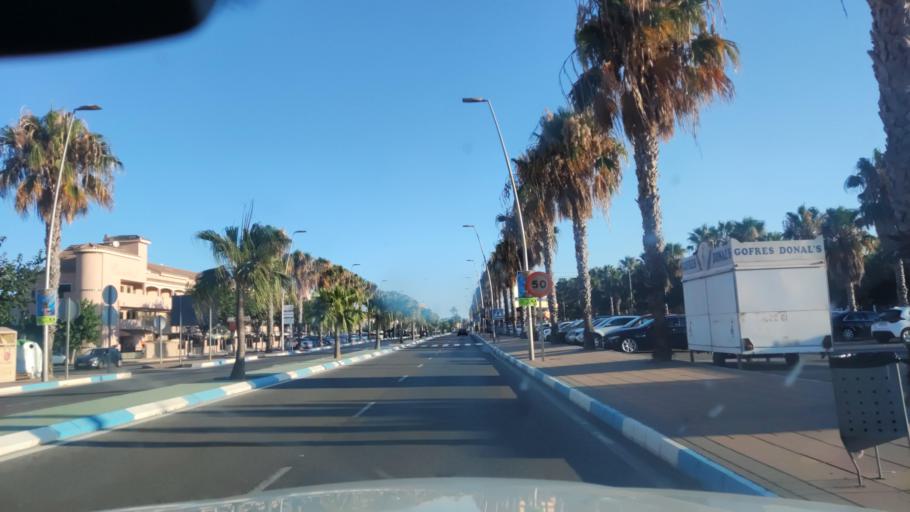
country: ES
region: Murcia
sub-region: Murcia
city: Los Alcazares
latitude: 37.7544
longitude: -0.8468
